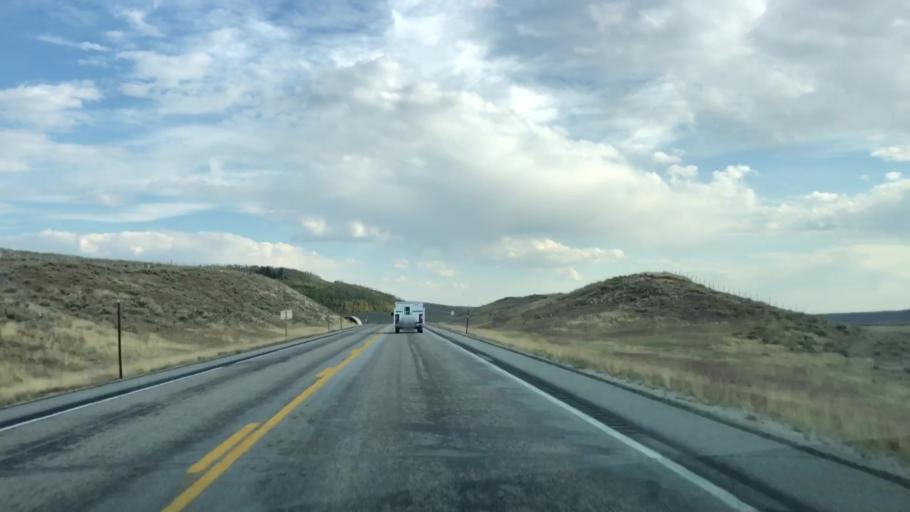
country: US
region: Wyoming
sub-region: Sublette County
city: Pinedale
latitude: 43.0927
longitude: -110.1658
